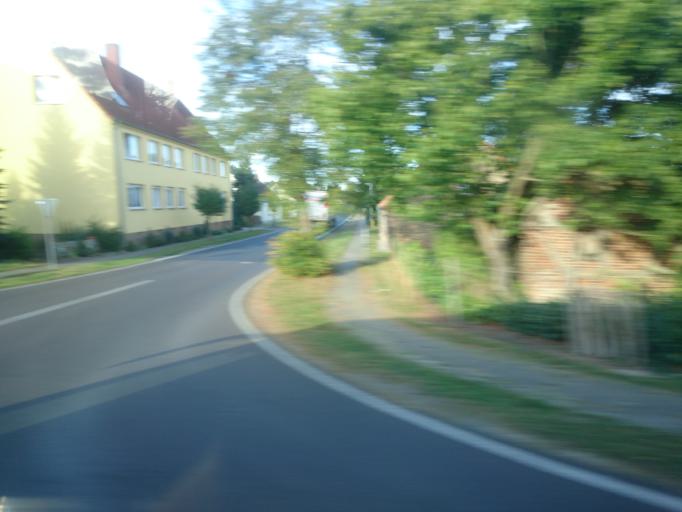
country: DE
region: Mecklenburg-Vorpommern
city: Anklam
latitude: 53.8881
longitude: 13.6722
